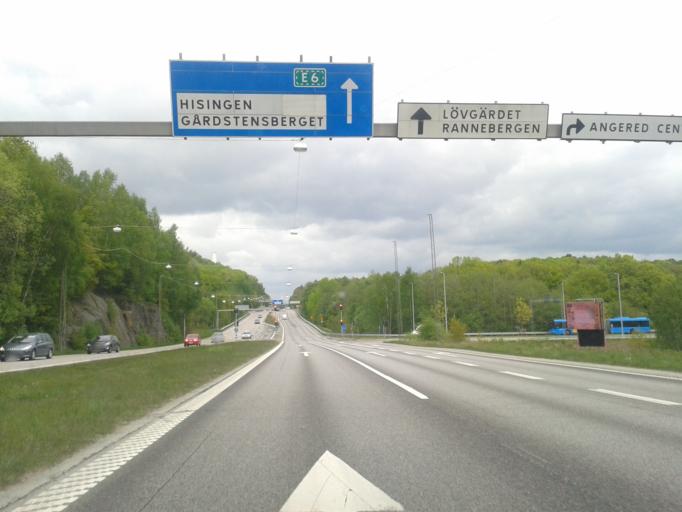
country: SE
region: Vaestra Goetaland
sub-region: Goteborg
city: Hammarkullen
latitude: 57.7936
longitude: 12.0425
